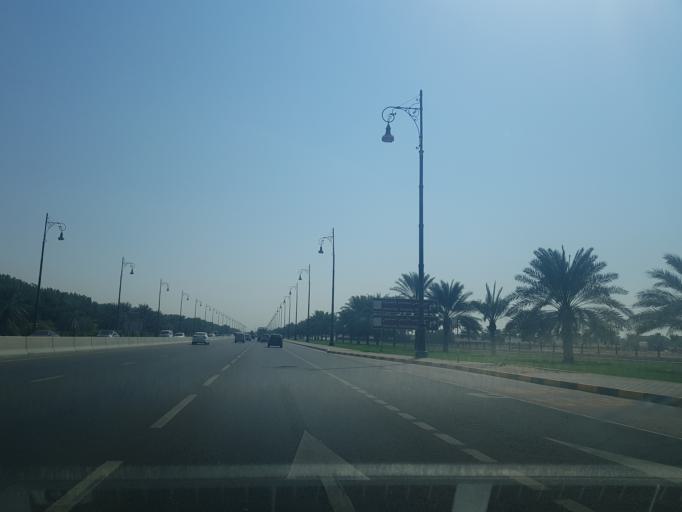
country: AE
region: Ash Shariqah
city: Sharjah
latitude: 25.3212
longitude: 55.5029
